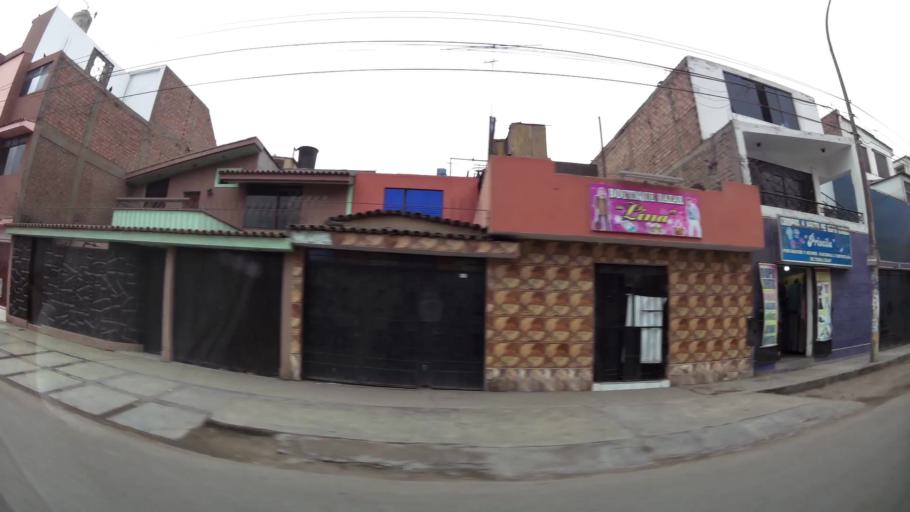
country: PE
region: Lima
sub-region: Lima
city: Urb. Santo Domingo
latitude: -11.9029
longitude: -77.0378
